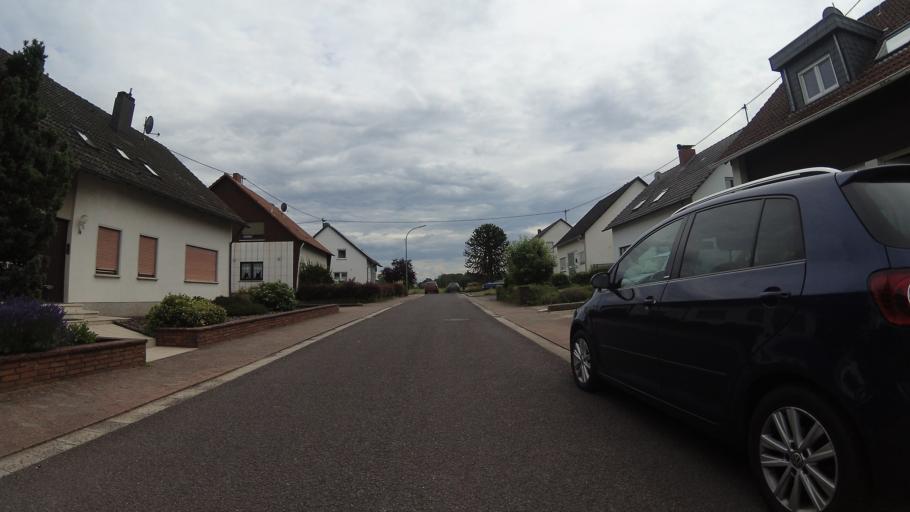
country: DE
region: Saarland
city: Wallerfangen
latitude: 49.3244
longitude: 6.7051
